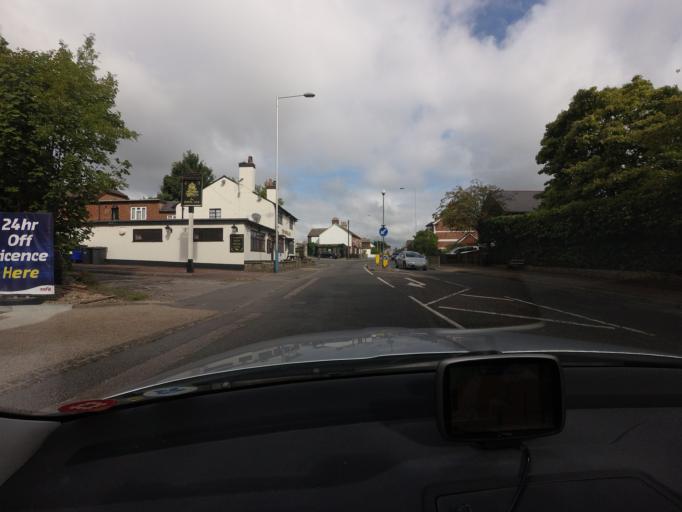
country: GB
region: England
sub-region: Kent
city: Tonbridge
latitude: 51.2053
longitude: 0.2773
